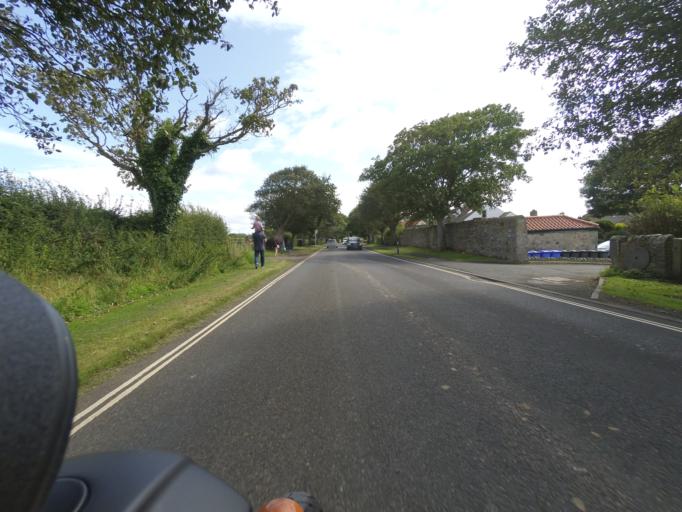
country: GB
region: England
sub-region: Northumberland
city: Bamburgh
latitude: 55.6071
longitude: -1.7253
